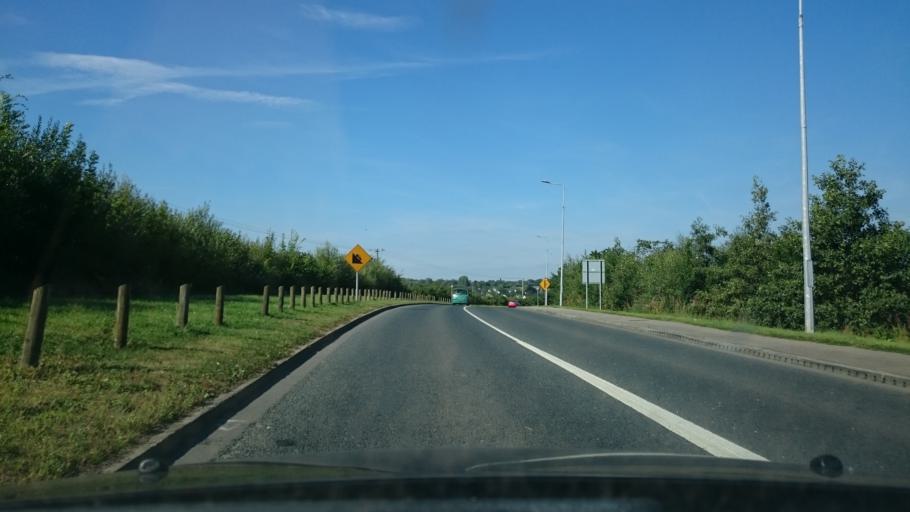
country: IE
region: Leinster
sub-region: Kilkenny
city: Graiguenamanagh
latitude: 52.5401
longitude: -6.9639
